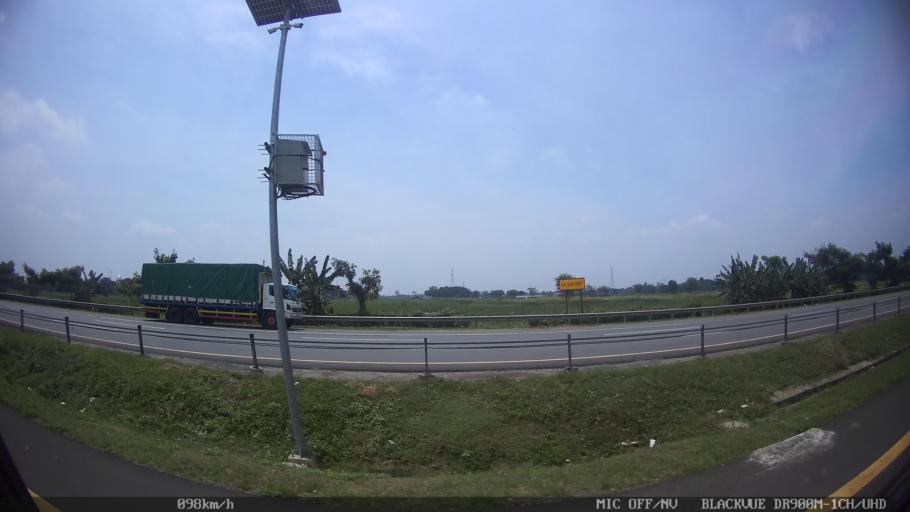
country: ID
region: West Java
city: Kresek
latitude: -6.1771
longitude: 106.3653
